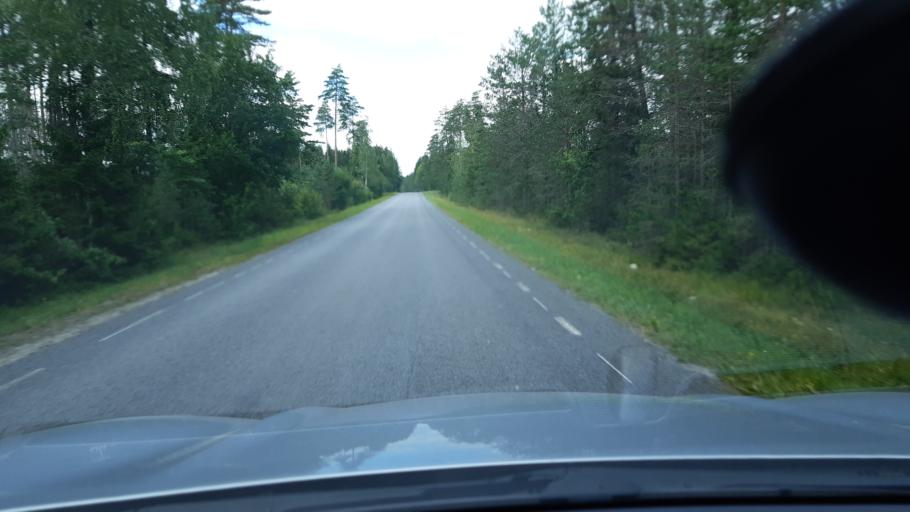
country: EE
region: Raplamaa
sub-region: Rapla vald
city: Rapla
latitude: 58.9049
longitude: 24.6800
